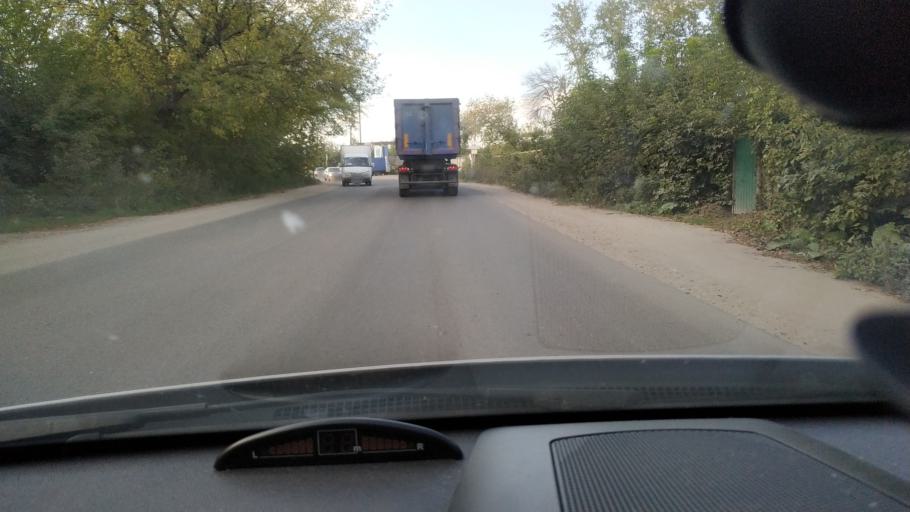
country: RU
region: Rjazan
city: Ryazan'
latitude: 54.6636
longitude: 39.6278
